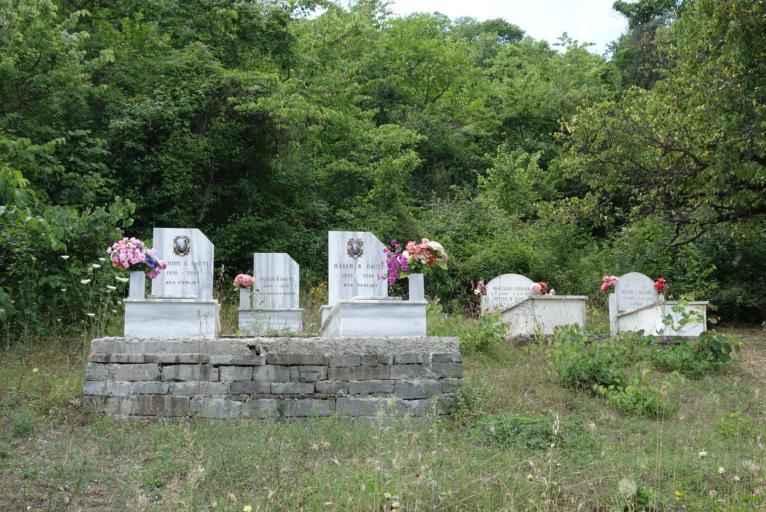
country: AL
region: Gjirokaster
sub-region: Rrethi i Permetit
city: Frasher
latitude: 40.2975
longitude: 20.4696
